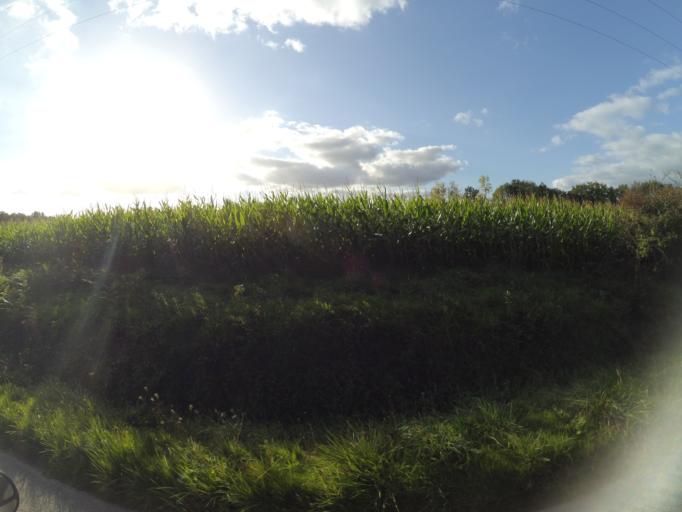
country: FR
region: Brittany
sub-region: Departement du Morbihan
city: Peillac
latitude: 47.7166
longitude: -2.1849
